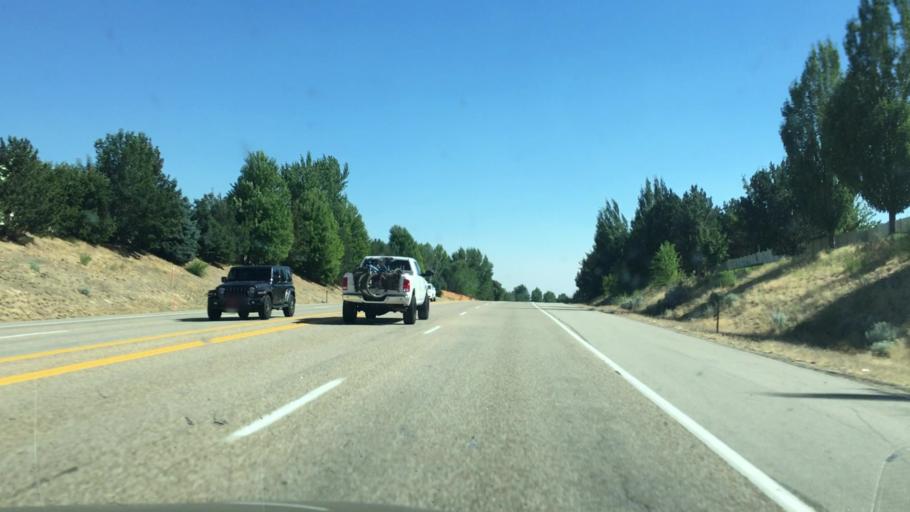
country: US
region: Idaho
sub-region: Ada County
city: Eagle
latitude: 43.7158
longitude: -116.3193
